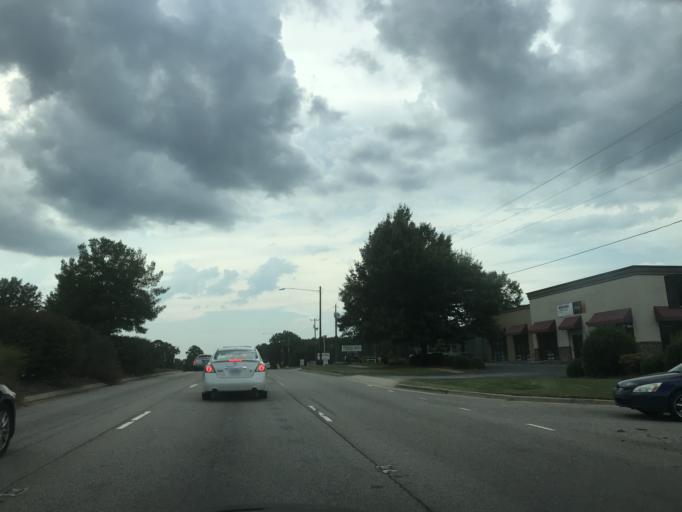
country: US
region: North Carolina
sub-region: Wake County
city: West Raleigh
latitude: 35.8614
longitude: -78.7100
